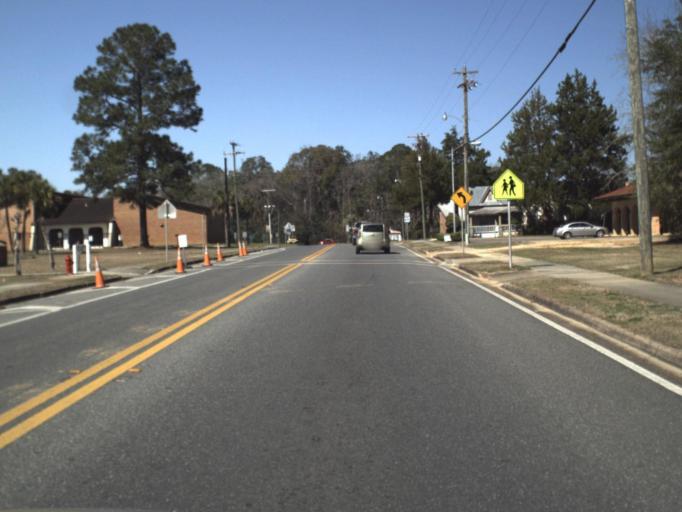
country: US
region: Florida
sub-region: Calhoun County
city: Blountstown
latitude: 30.4484
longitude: -85.0457
